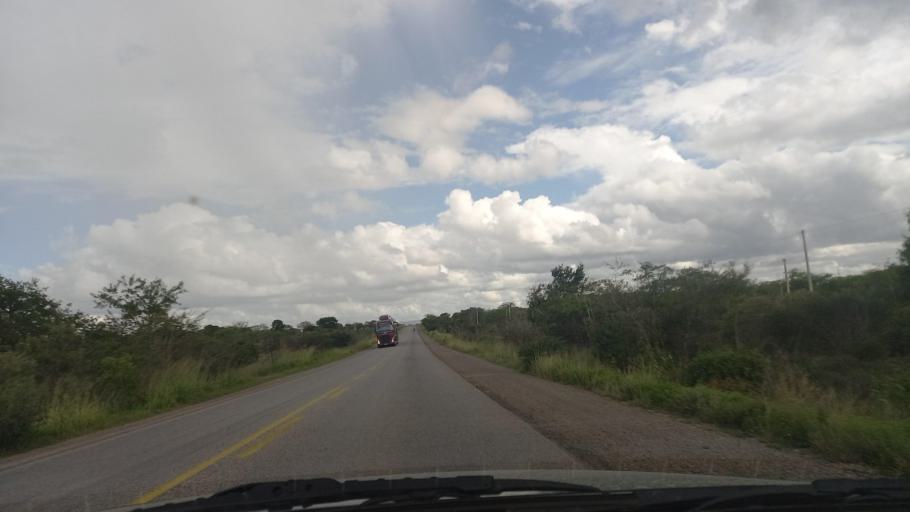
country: BR
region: Pernambuco
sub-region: Cachoeirinha
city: Cachoeirinha
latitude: -8.5410
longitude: -36.2687
